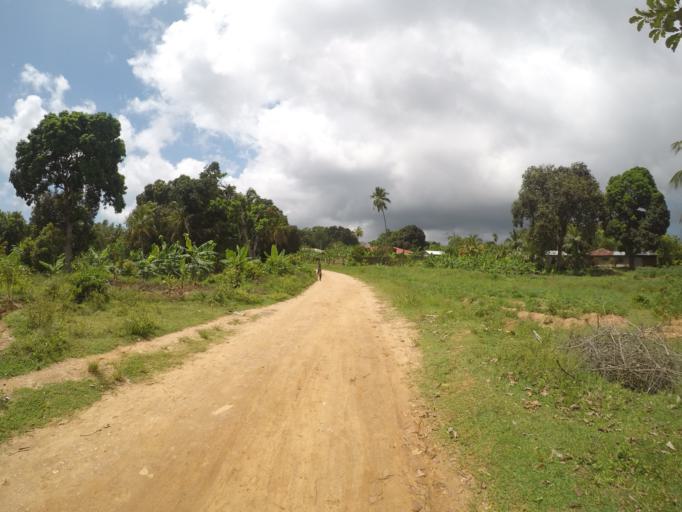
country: TZ
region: Pemba South
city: Mtambile
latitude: -5.3893
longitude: 39.7393
